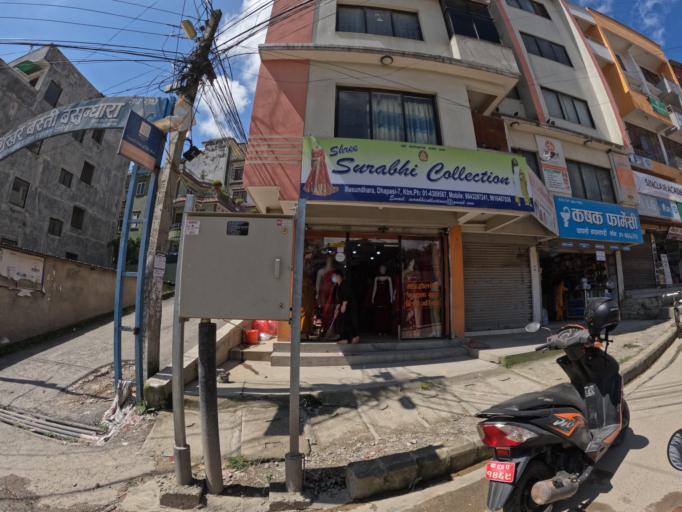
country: NP
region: Central Region
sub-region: Bagmati Zone
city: Kathmandu
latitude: 27.7442
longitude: 85.3296
